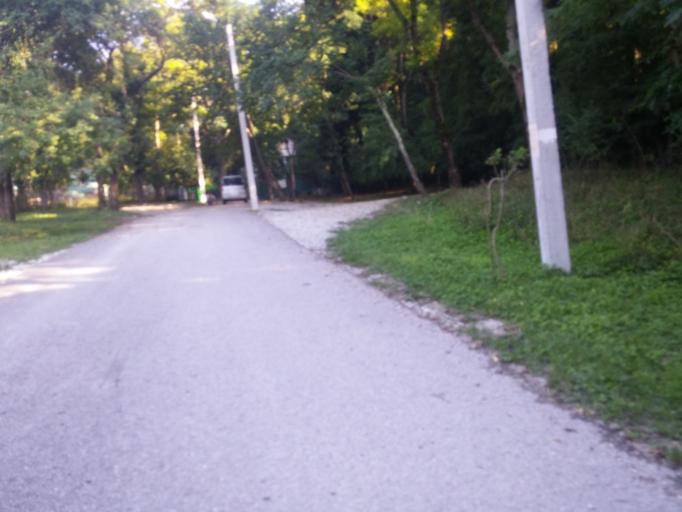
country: RU
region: Krasnodarskiy
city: Divnomorskoye
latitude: 44.4673
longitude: 38.1647
